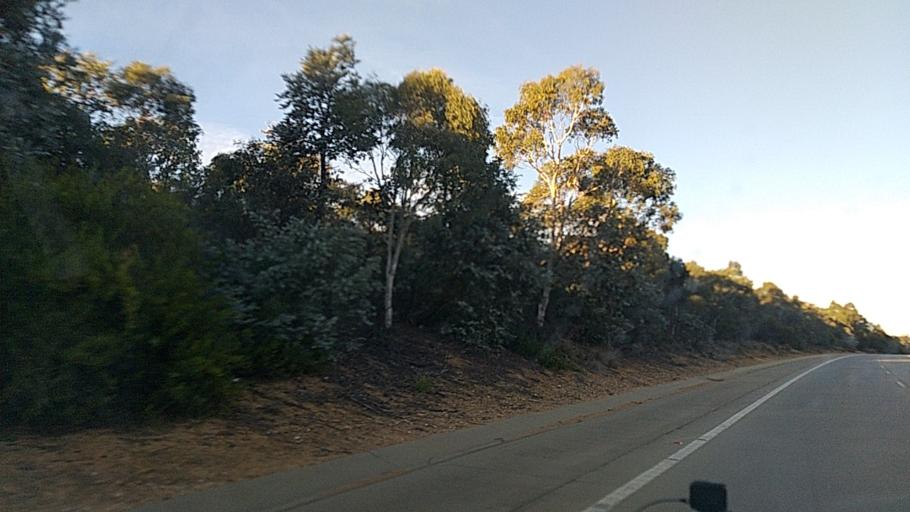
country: AU
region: New South Wales
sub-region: Yass Valley
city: Gundaroo
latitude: -35.1099
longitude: 149.3685
